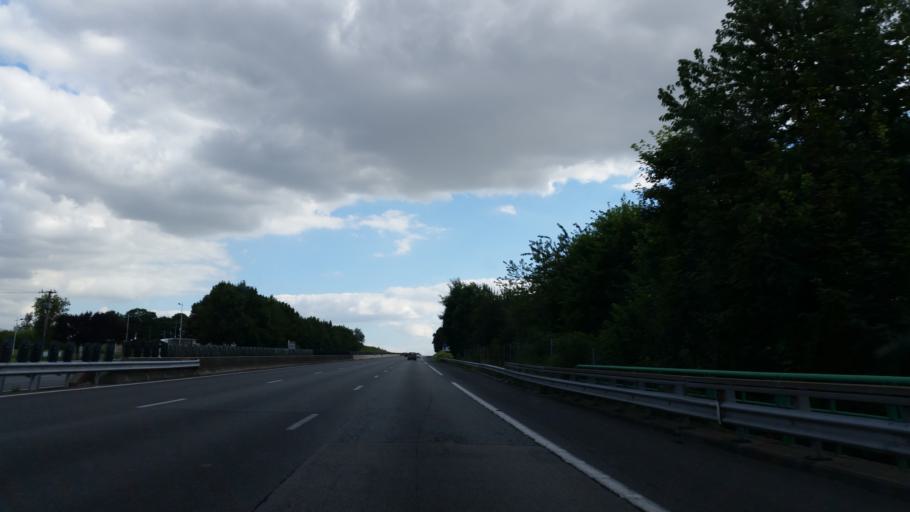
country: FR
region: Nord-Pas-de-Calais
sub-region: Departement du Pas-de-Calais
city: Croisilles
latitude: 50.1930
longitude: 2.8709
